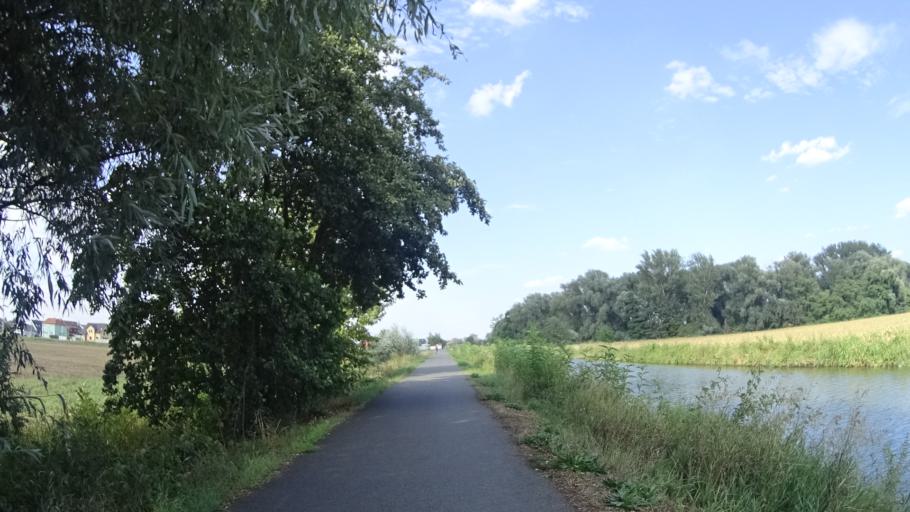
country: CZ
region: Zlin
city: Babice
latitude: 49.1153
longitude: 17.4833
